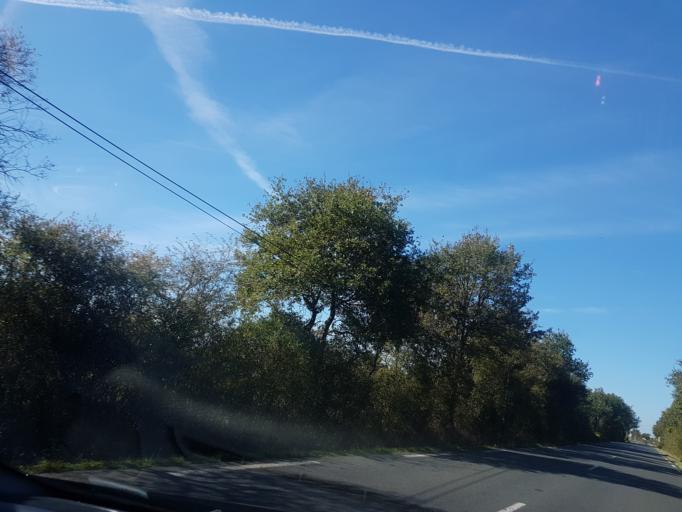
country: FR
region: Pays de la Loire
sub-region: Departement de la Loire-Atlantique
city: Casson
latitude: 47.4277
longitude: -1.5971
